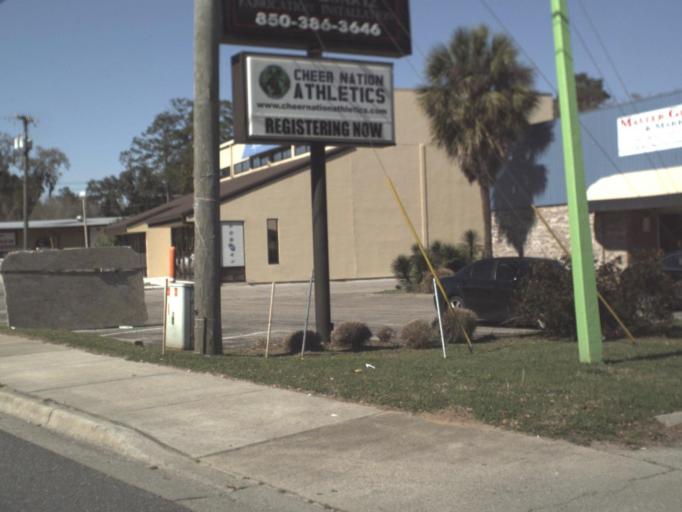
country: US
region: Florida
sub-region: Leon County
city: Tallahassee
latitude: 30.4870
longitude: -84.2381
